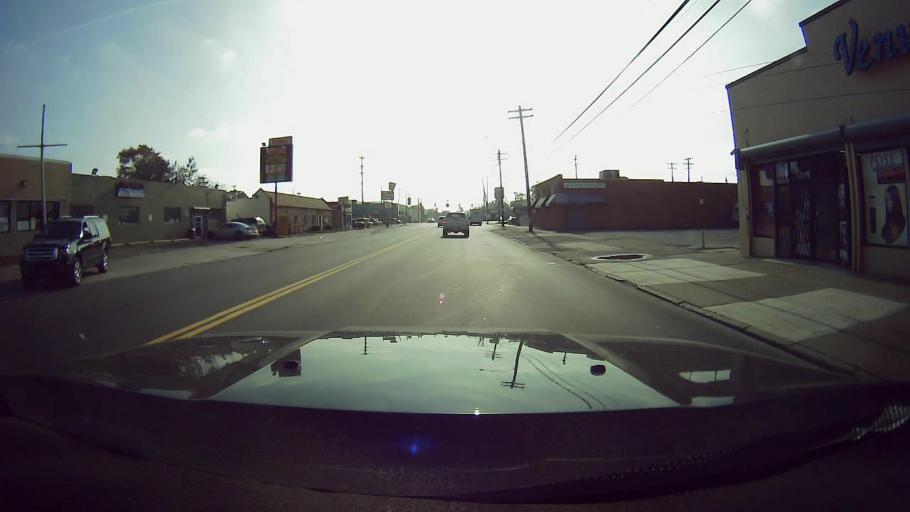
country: US
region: Michigan
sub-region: Oakland County
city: Oak Park
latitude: 42.4178
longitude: -83.1799
